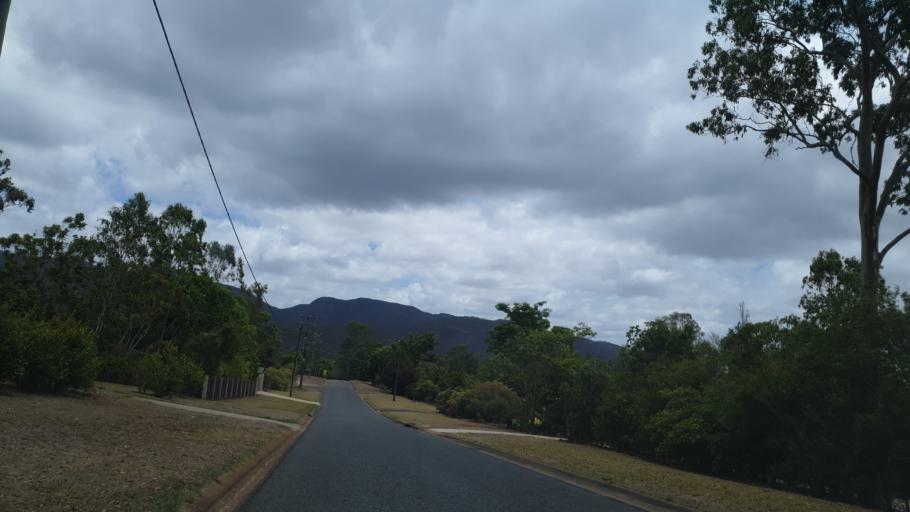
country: AU
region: Queensland
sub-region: Tablelands
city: Tolga
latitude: -17.2098
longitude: 145.4496
